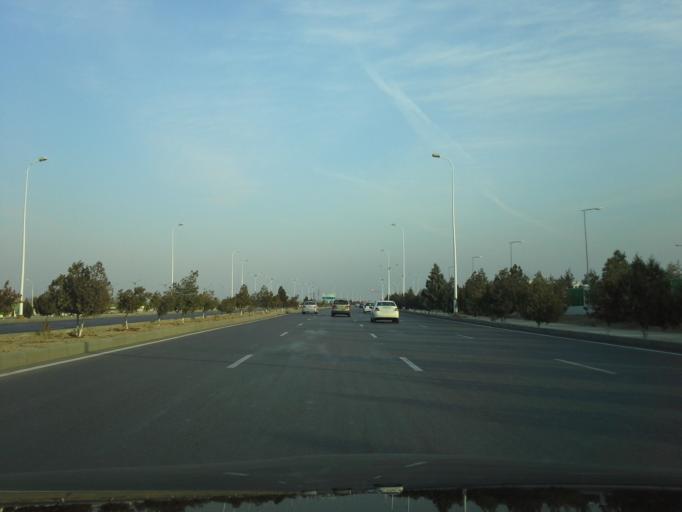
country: TM
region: Ahal
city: Abadan
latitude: 38.0476
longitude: 58.1969
